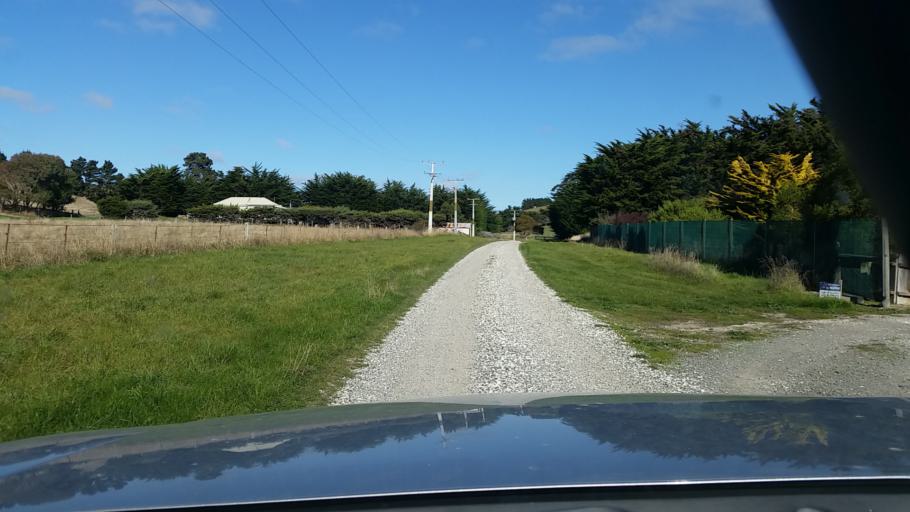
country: NZ
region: Marlborough
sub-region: Marlborough District
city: Blenheim
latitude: -41.7401
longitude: 174.1666
